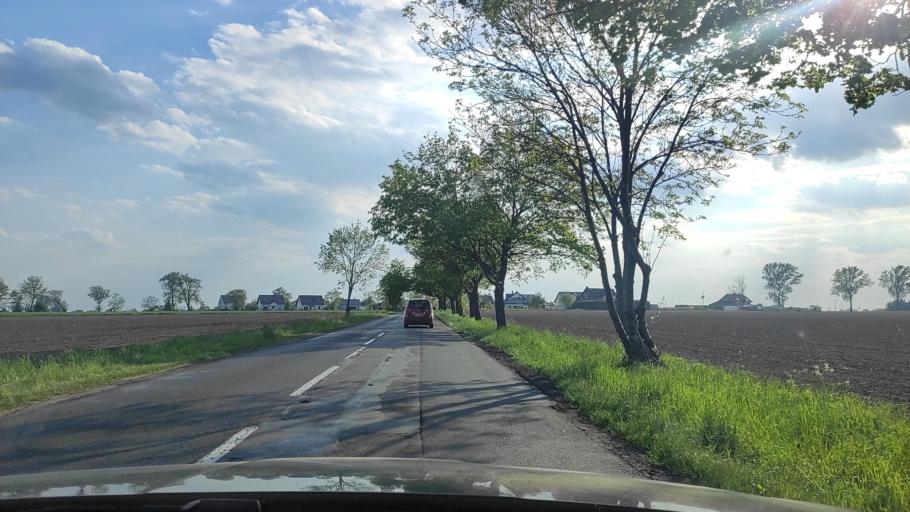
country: PL
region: Greater Poland Voivodeship
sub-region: Powiat poznanski
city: Kleszczewo
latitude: 52.3092
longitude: 17.1384
